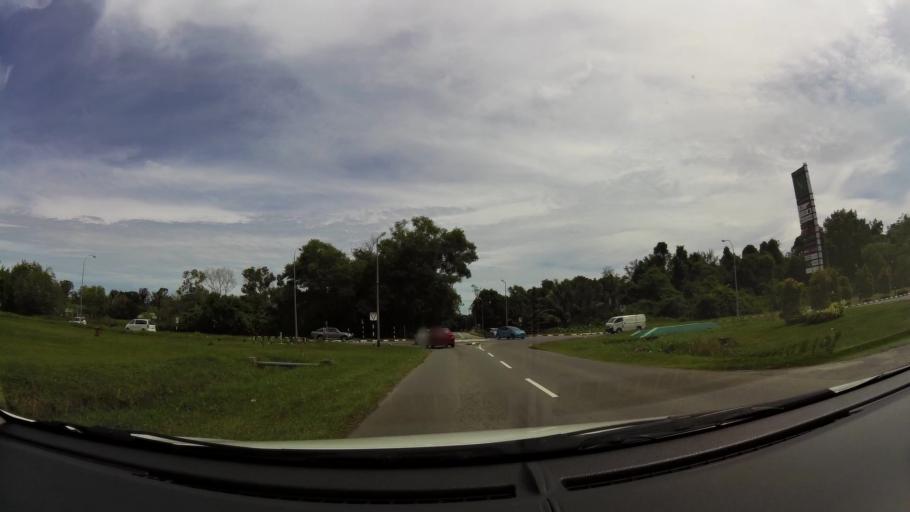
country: BN
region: Belait
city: Seria
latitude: 4.6005
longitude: 114.2861
